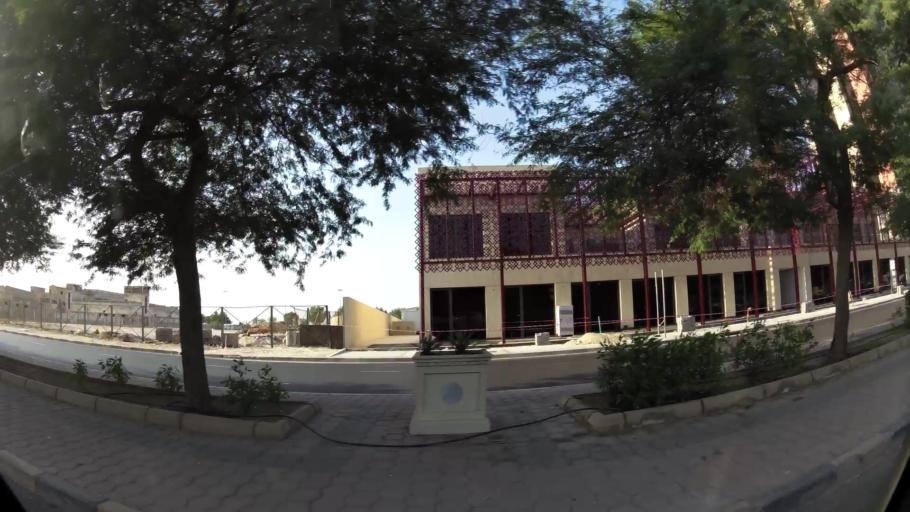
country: KW
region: Muhafazat Hawalli
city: As Salimiyah
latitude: 29.3451
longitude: 48.0839
